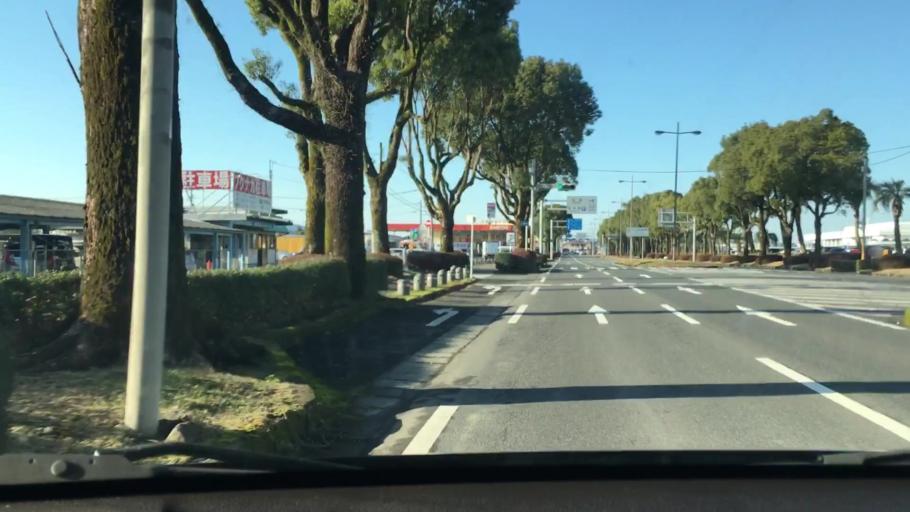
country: JP
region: Kagoshima
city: Kajiki
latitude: 31.7988
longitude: 130.7158
